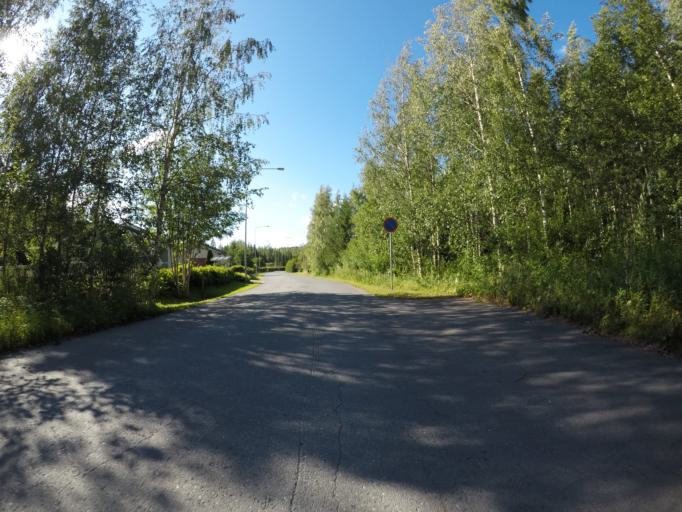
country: FI
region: Haeme
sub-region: Haemeenlinna
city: Haemeenlinna
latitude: 61.0201
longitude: 24.5133
